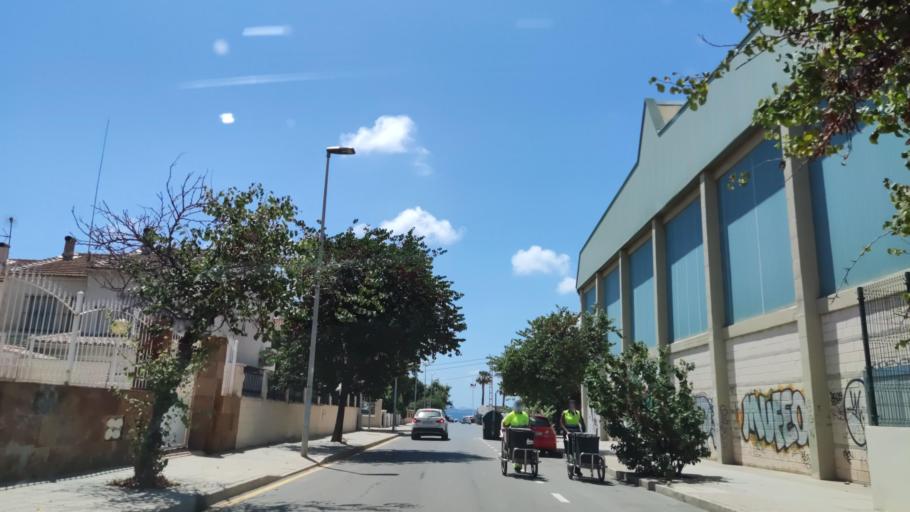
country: ES
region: Murcia
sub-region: Murcia
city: Los Alcazares
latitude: 37.7546
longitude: -0.8379
